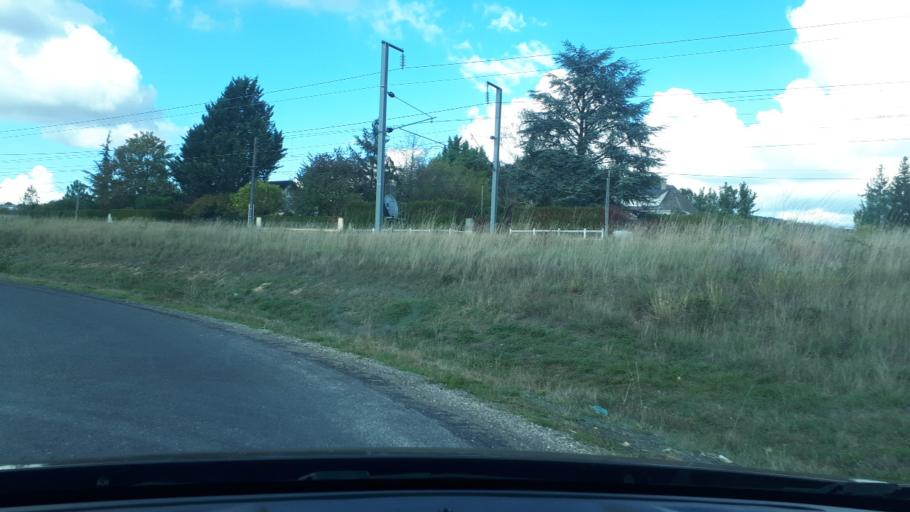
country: FR
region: Centre
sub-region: Departement du Loir-et-Cher
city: Mareuil-sur-Cher
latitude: 47.3027
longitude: 1.3508
